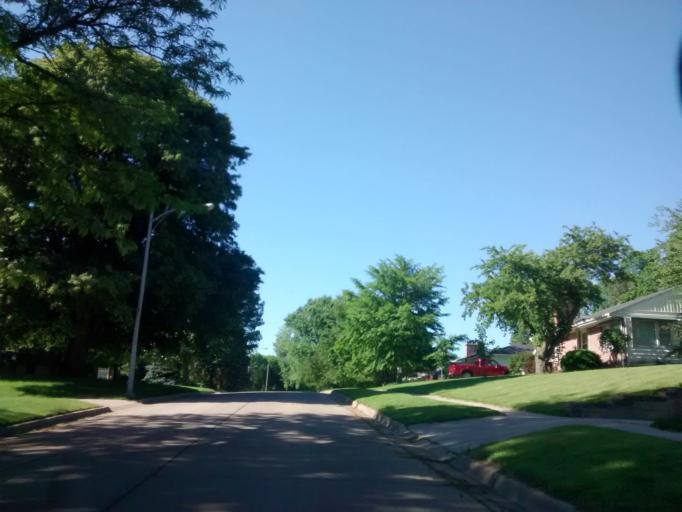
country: US
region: Nebraska
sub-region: Douglas County
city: Ralston
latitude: 41.2563
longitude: -96.0195
